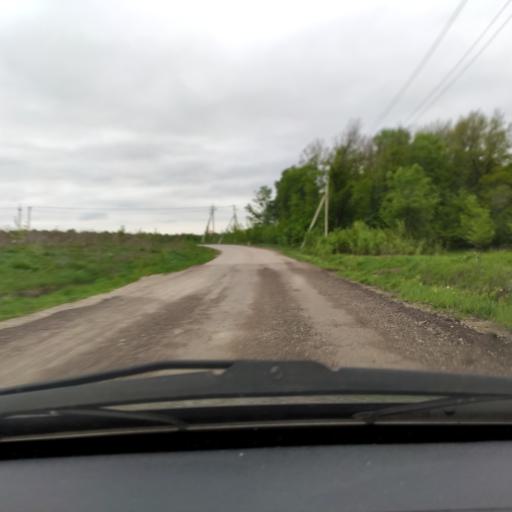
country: RU
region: Bashkortostan
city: Kabakovo
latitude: 54.6209
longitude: 56.1594
